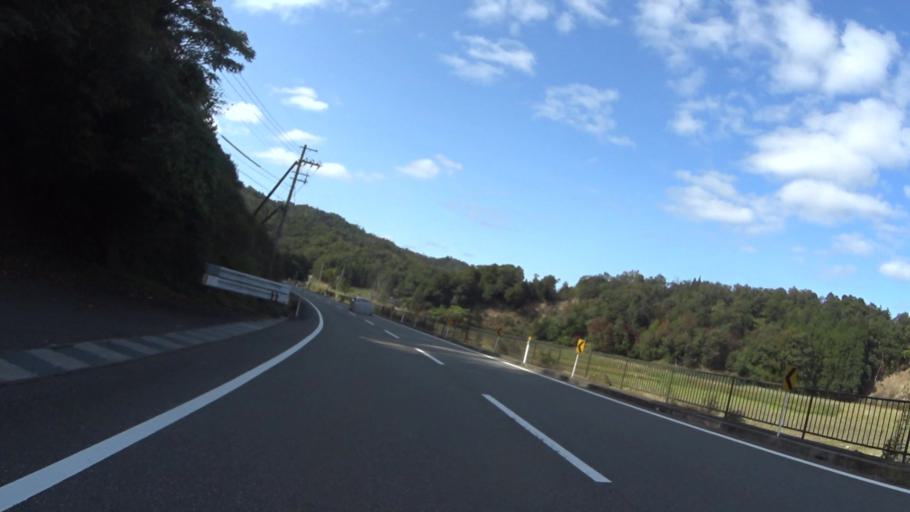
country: JP
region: Hyogo
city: Toyooka
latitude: 35.5644
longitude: 134.9777
